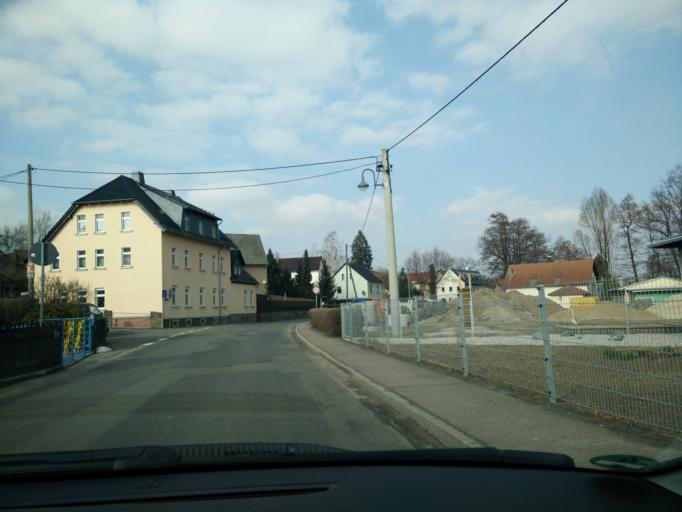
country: DE
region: Saxony
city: Colditz
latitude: 51.1177
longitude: 12.7866
